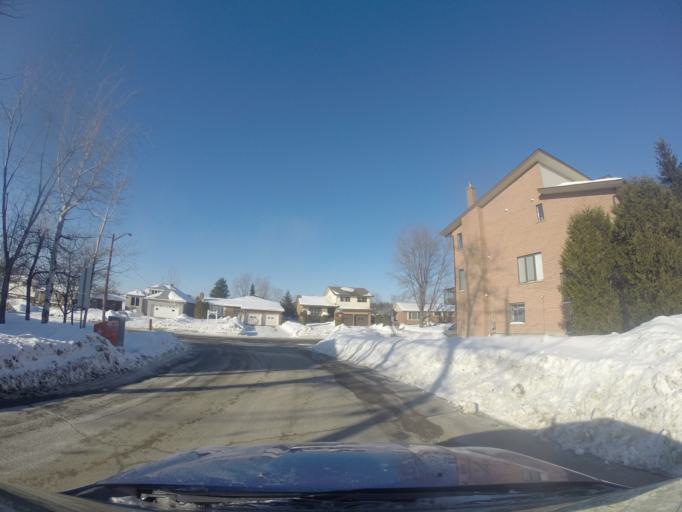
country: CA
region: Ontario
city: Greater Sudbury
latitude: 46.4640
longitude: -80.9883
